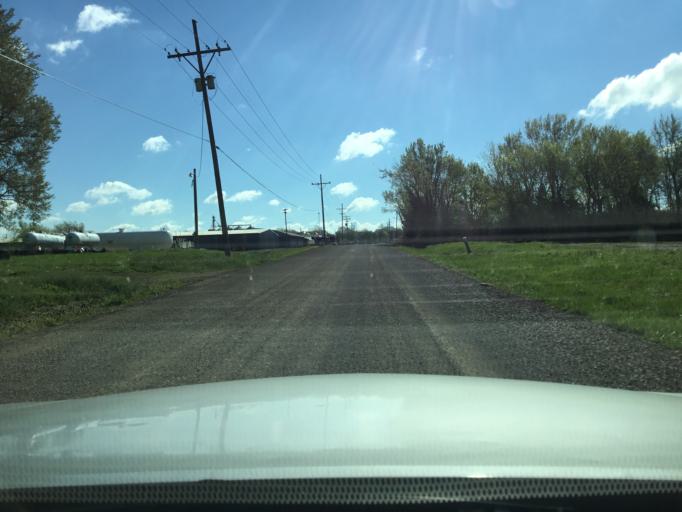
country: US
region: Kansas
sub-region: Allen County
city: Iola
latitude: 37.9285
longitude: -95.4156
